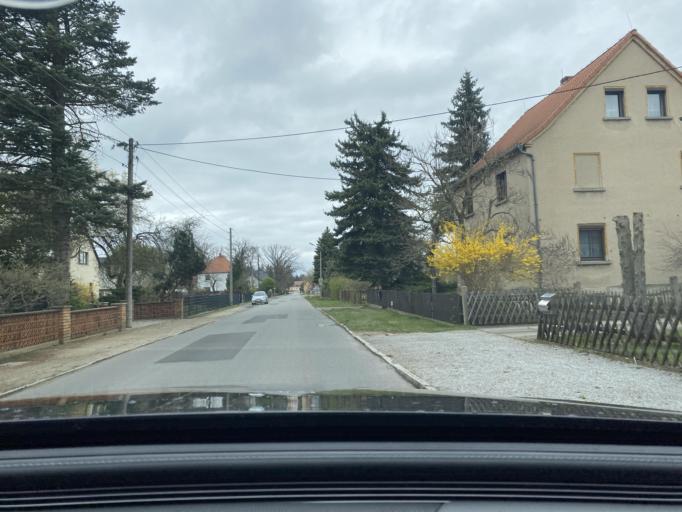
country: DE
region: Saxony
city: Neschwitz
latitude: 51.2650
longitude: 14.3300
